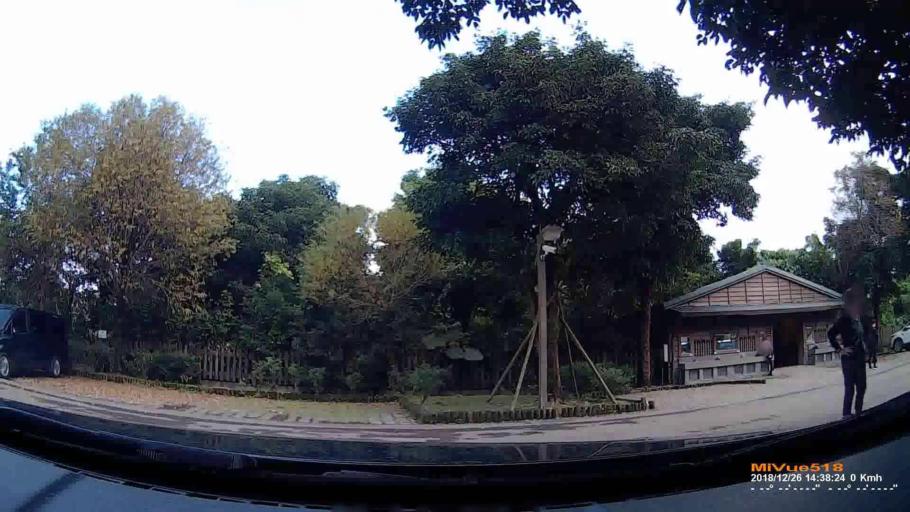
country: TW
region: Taiwan
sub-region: Yilan
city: Yilan
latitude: 24.6807
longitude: 121.7703
